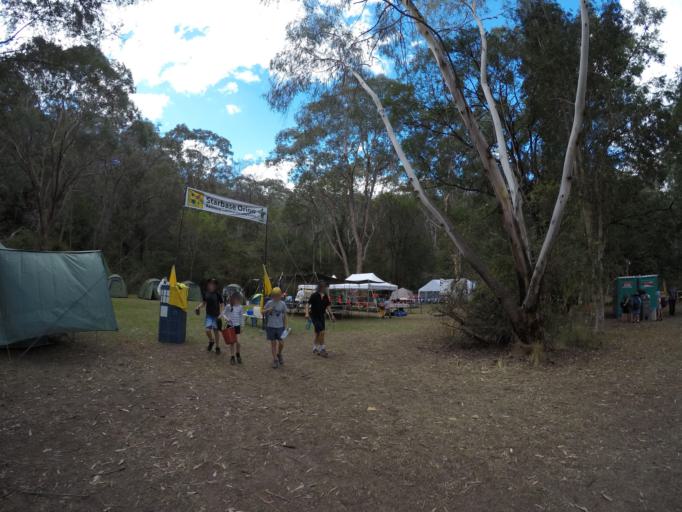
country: AU
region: New South Wales
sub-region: Hawkesbury
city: Pitt Town
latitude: -33.4696
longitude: 150.8907
